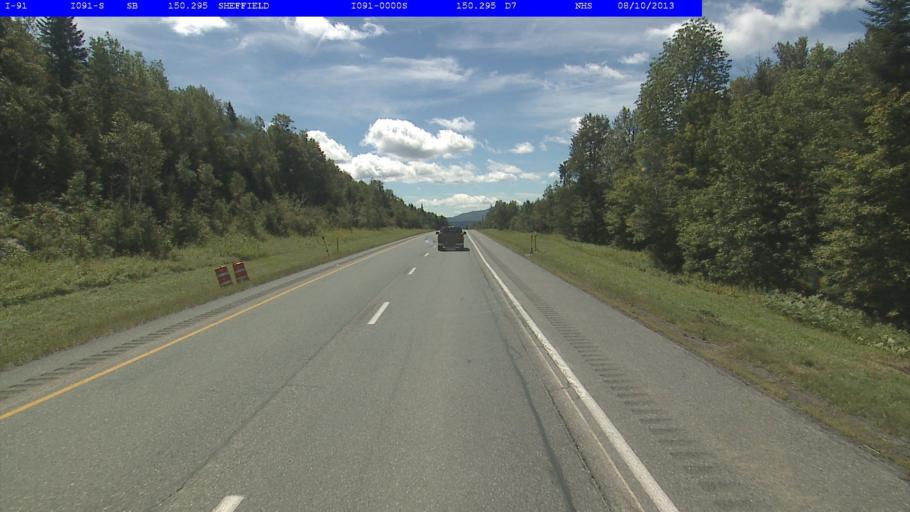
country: US
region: Vermont
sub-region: Caledonia County
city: Lyndonville
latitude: 44.6689
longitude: -72.1333
